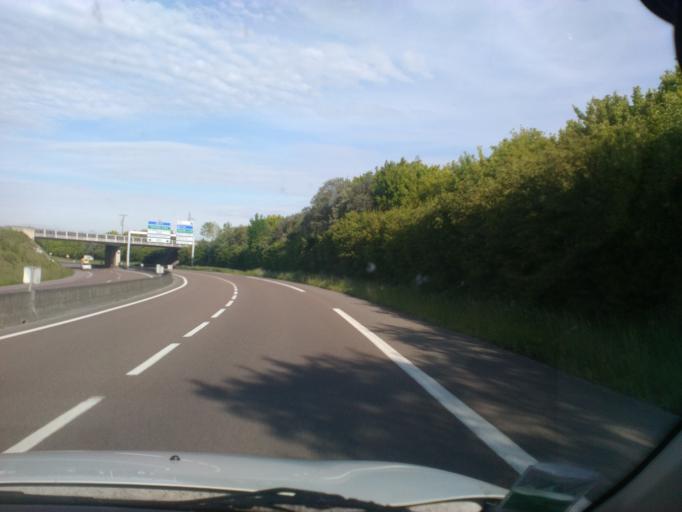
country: FR
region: Champagne-Ardenne
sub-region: Departement de l'Aube
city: Pont-Sainte-Marie
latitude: 48.3354
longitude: 4.1065
